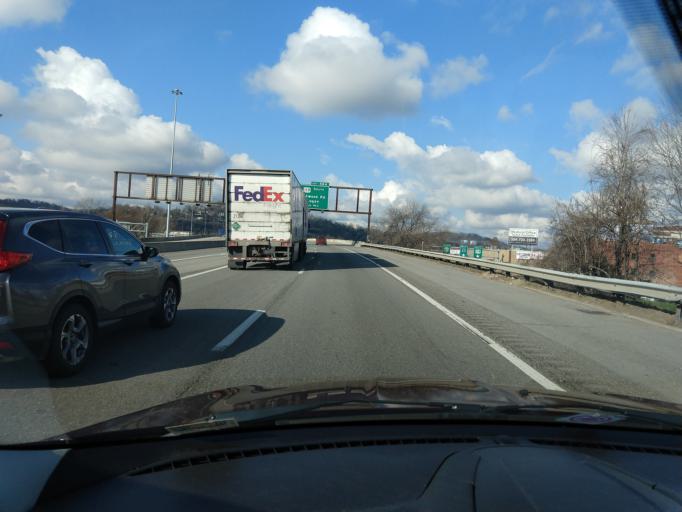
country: US
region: West Virginia
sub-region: Kanawha County
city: Charleston
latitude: 38.3595
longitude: -81.6389
